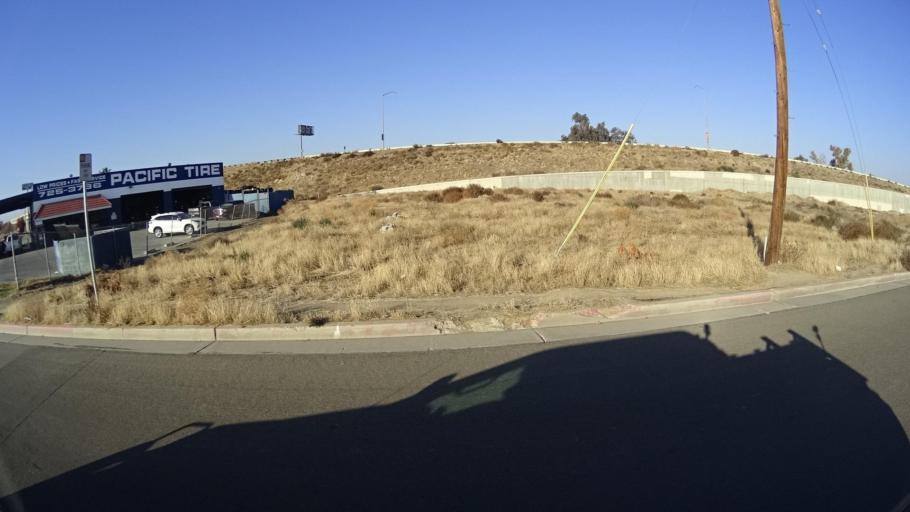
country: US
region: California
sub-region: Kern County
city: Delano
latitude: 35.7857
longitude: -119.2497
